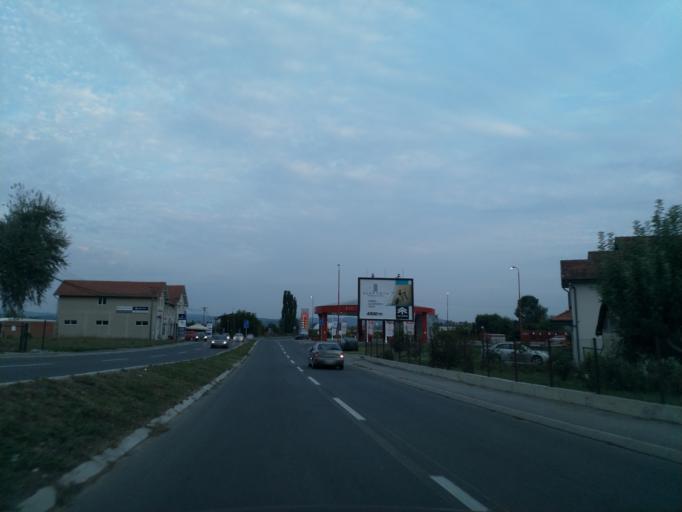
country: RS
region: Central Serbia
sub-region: Sumadijski Okrug
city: Kragujevac
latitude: 44.0449
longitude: 20.9075
